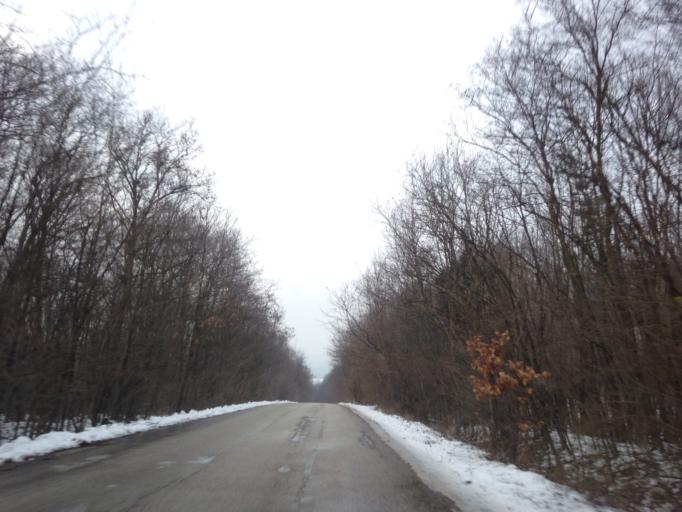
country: SK
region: Nitriansky
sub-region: Okres Nitra
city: Vrable
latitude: 48.0964
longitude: 18.3642
